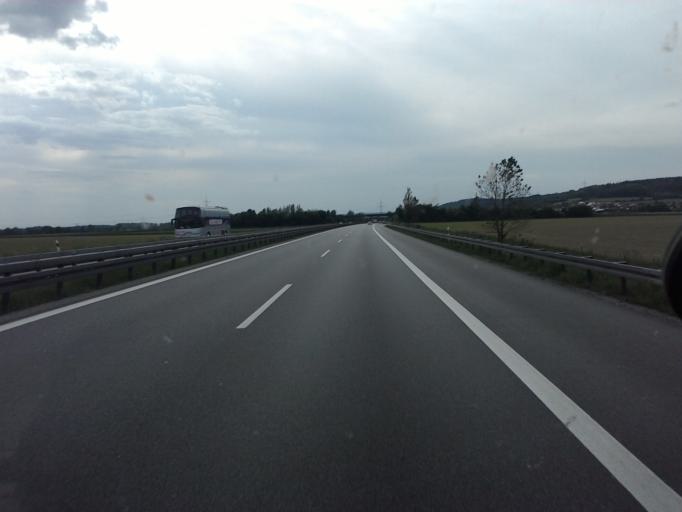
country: DE
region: Bavaria
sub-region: Lower Bavaria
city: Aholfing
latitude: 48.9748
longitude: 12.4836
